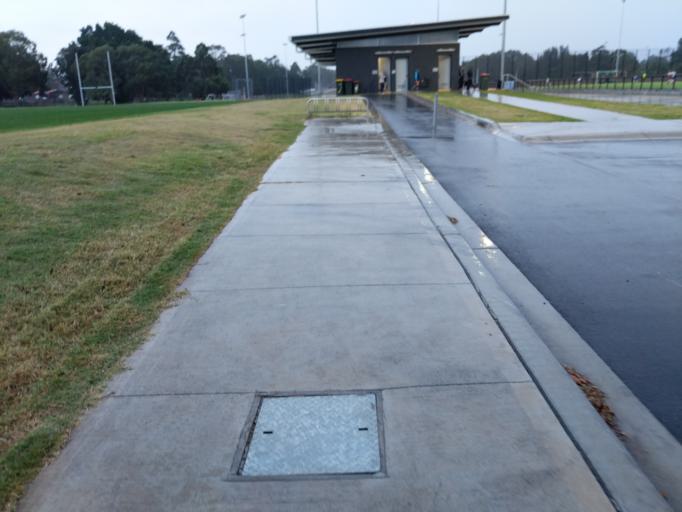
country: AU
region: New South Wales
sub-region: Ashfield
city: Croydon
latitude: -33.8668
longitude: 151.1098
